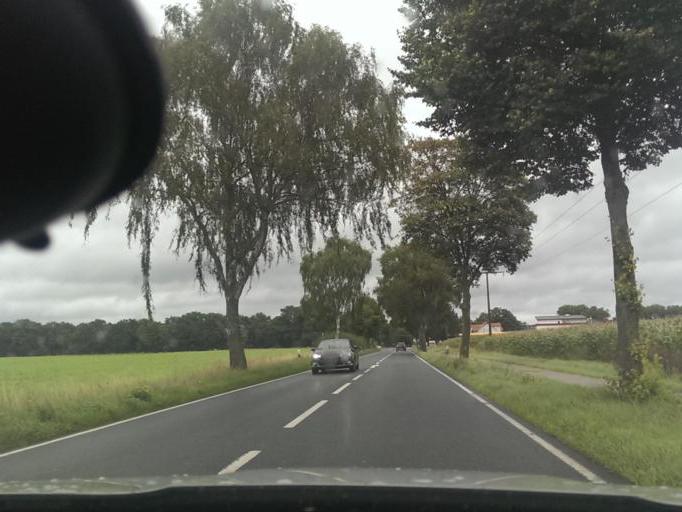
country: DE
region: Lower Saxony
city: Elze
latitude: 52.5527
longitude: 9.7719
